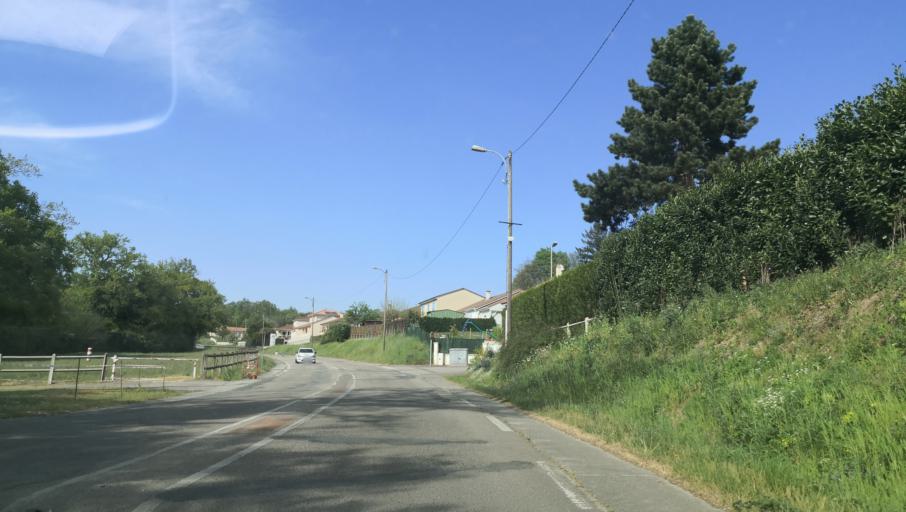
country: FR
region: Limousin
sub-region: Departement de la Haute-Vienne
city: Couzeix
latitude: 45.8623
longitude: 1.2586
